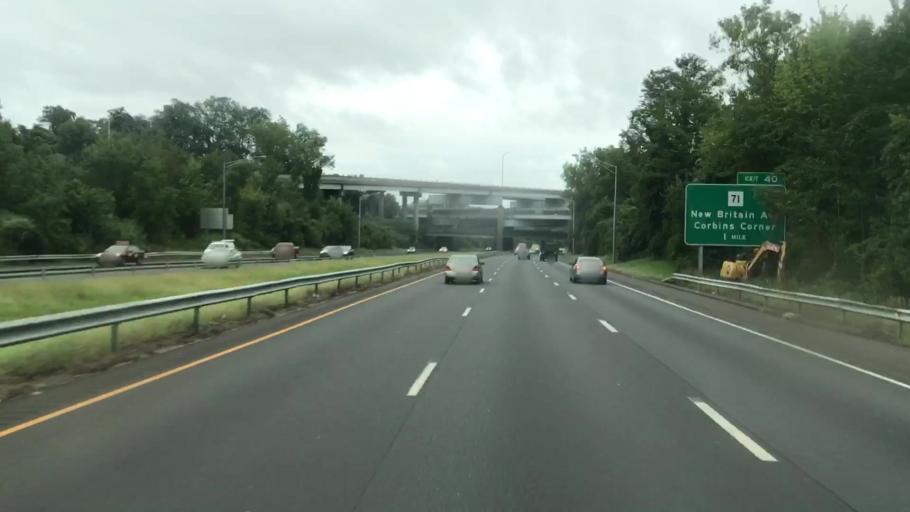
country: US
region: Connecticut
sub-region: Hartford County
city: West Hartford
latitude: 41.7248
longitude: -72.7774
